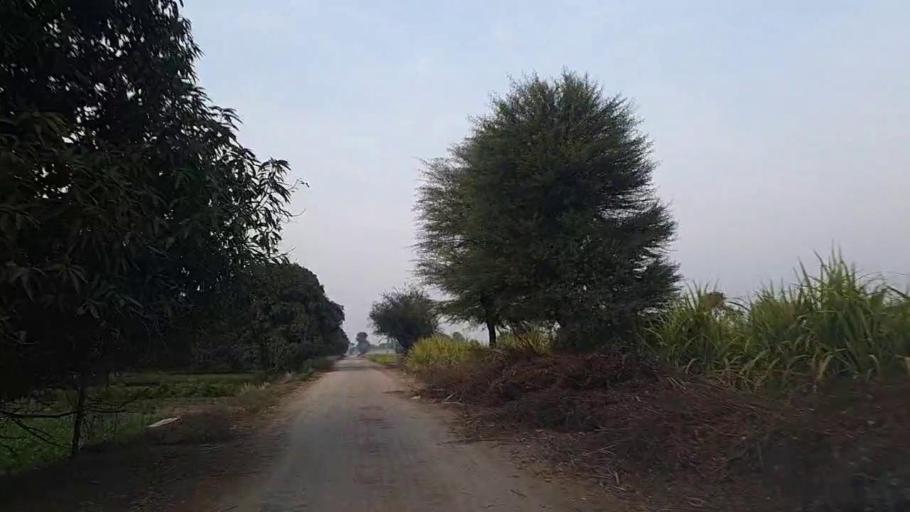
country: PK
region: Sindh
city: Jam Sahib
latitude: 26.4658
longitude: 68.5480
